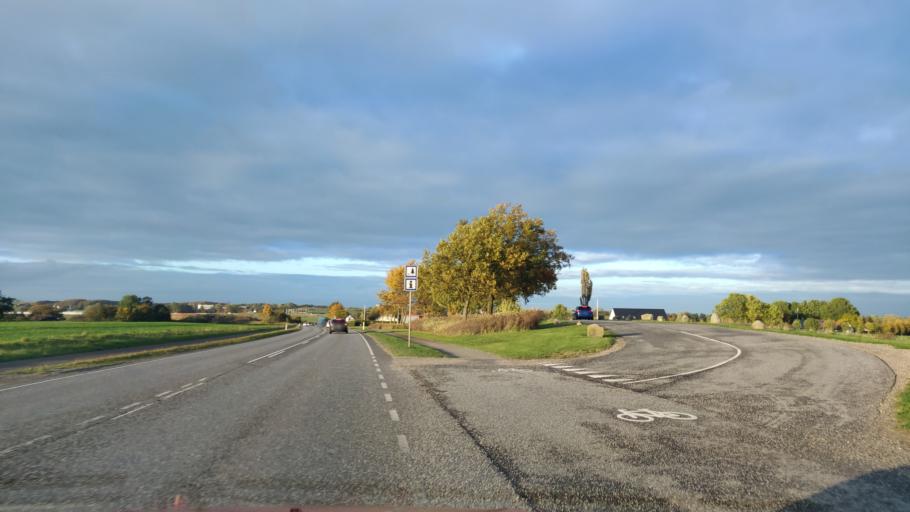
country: DK
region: Zealand
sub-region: Holbaek Kommune
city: Holbaek
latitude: 55.6767
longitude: 11.6908
